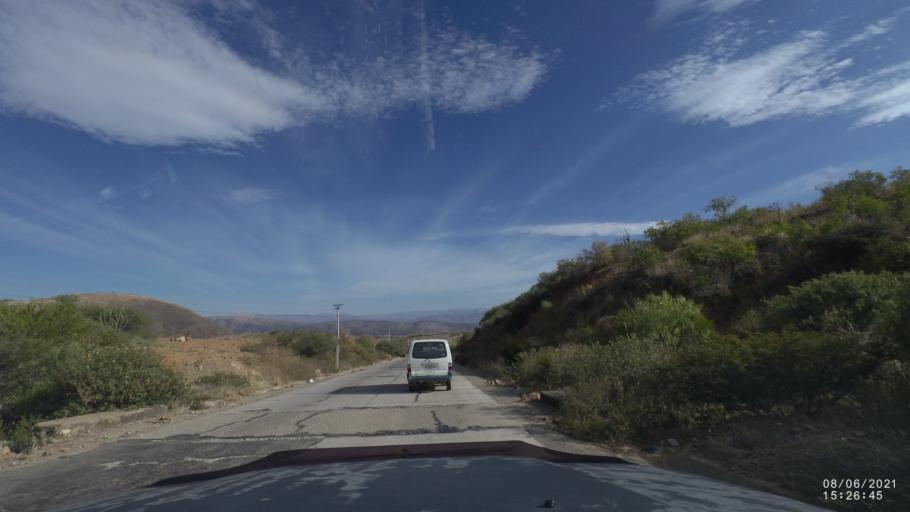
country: BO
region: Cochabamba
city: Cochabamba
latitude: -17.5321
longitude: -66.2006
